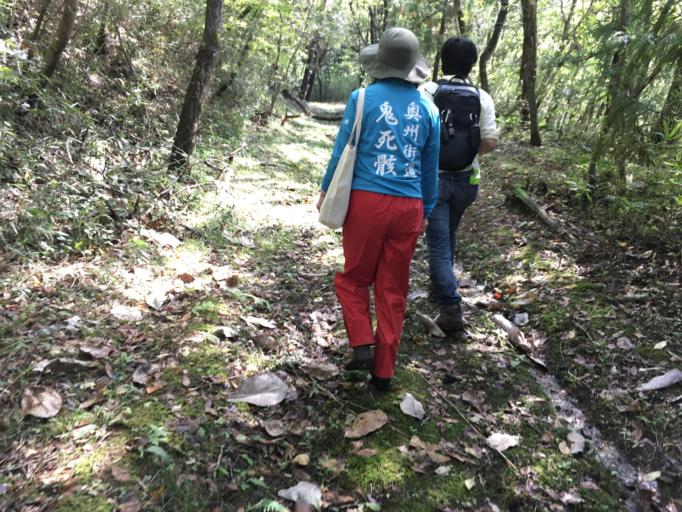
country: JP
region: Iwate
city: Ichinoseki
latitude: 38.8757
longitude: 141.1240
